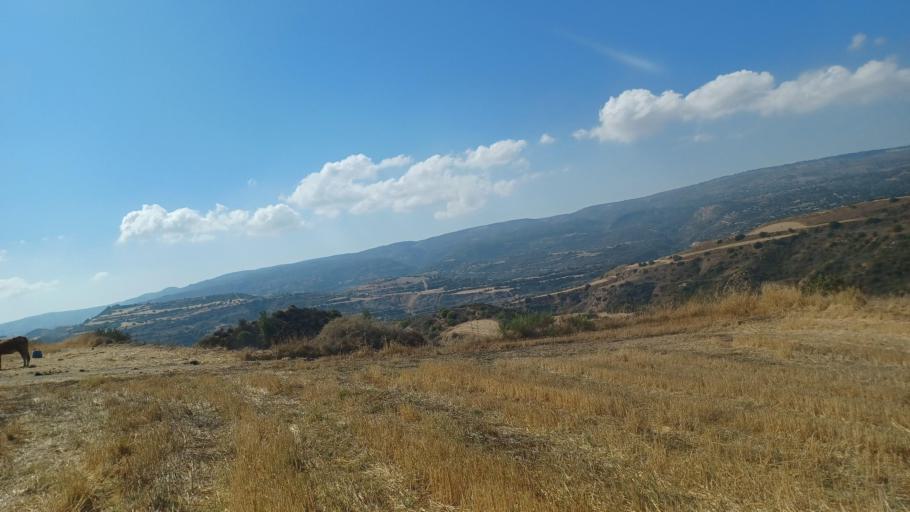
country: CY
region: Pafos
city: Polis
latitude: 34.9904
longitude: 32.4673
